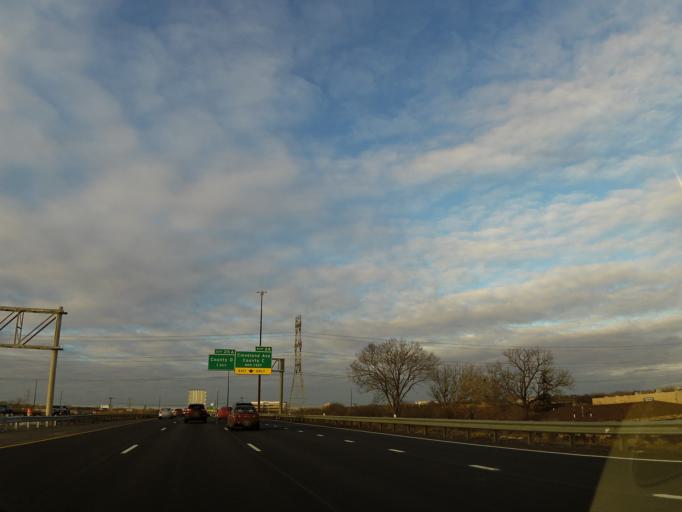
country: US
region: Minnesota
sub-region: Ramsey County
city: Lauderdale
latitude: 45.0182
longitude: -93.1884
